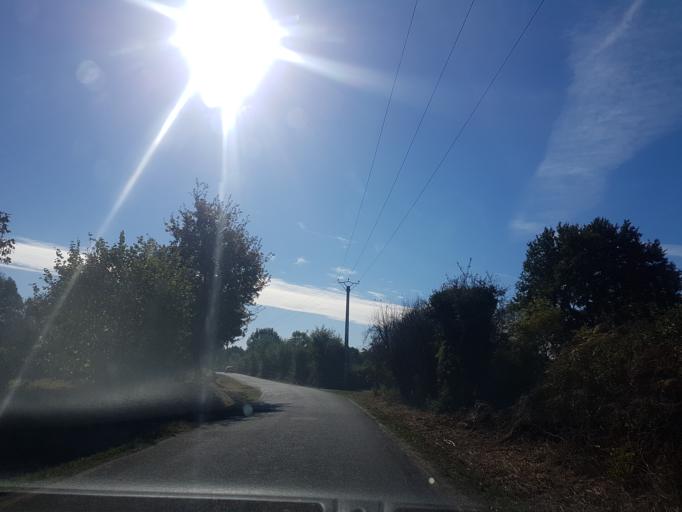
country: FR
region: Pays de la Loire
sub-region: Departement de la Loire-Atlantique
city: Petit-Mars
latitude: 47.3941
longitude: -1.4650
